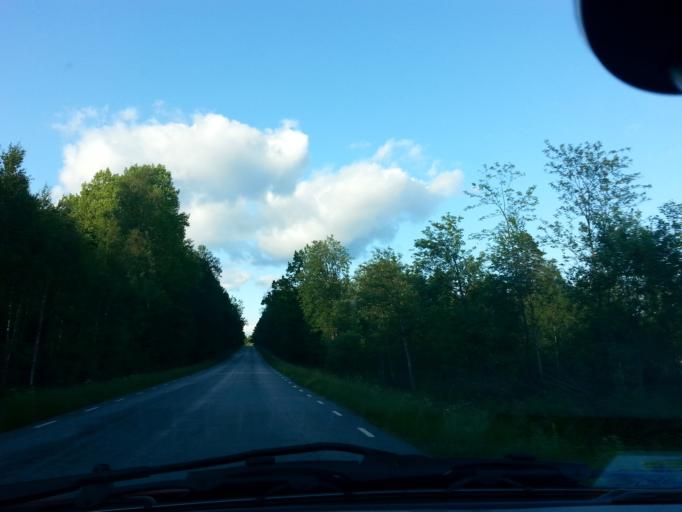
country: SE
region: Joenkoeping
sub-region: Gislaveds Kommun
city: Reftele
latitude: 57.2261
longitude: 13.6319
